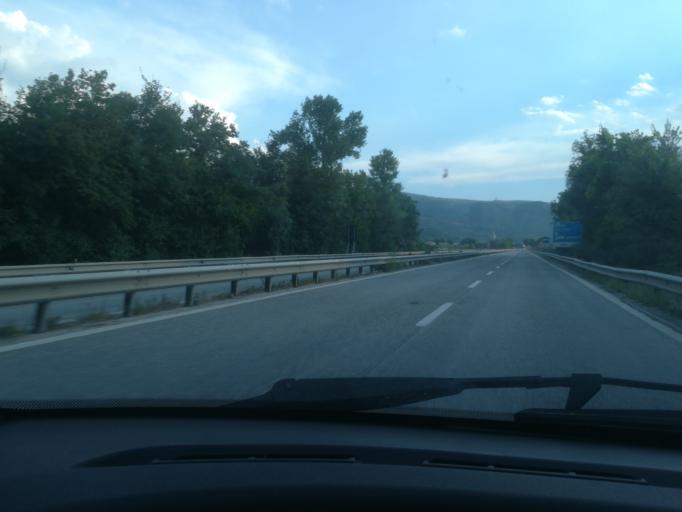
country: IT
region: The Marches
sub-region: Provincia di Macerata
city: Belforte del Chienti
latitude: 43.1565
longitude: 13.2380
